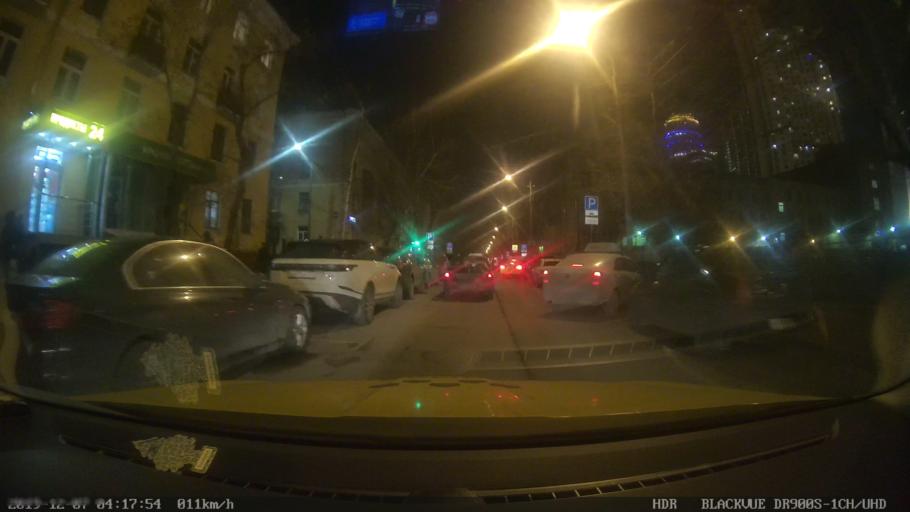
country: RU
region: Moskovskaya
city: Presnenskiy
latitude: 55.7748
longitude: 37.5454
